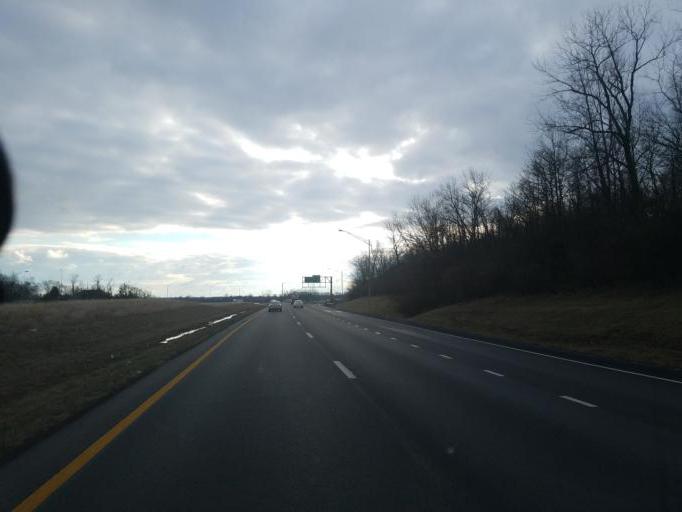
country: US
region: Missouri
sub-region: Saint Louis County
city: Glasgow Village
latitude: 38.7674
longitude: -90.1883
